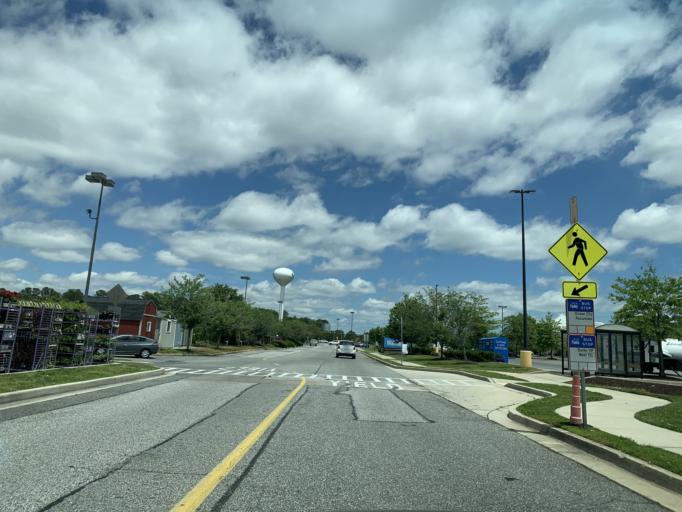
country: US
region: Maryland
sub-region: Worcester County
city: Ocean Pines
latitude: 38.3410
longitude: -75.1629
